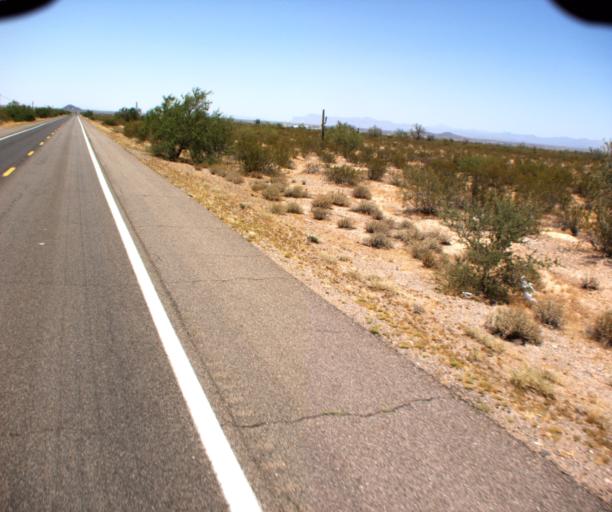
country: US
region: Arizona
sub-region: Pinal County
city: Florence
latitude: 32.9941
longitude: -111.3659
